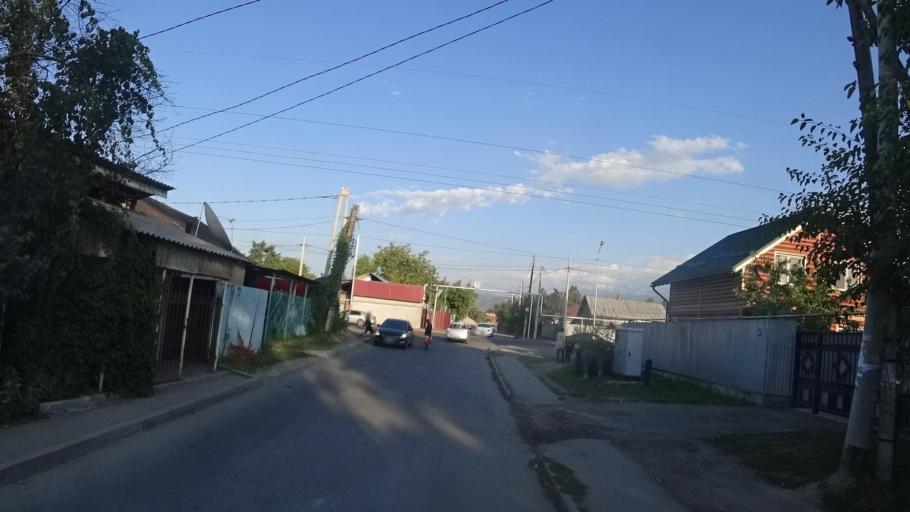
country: KZ
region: Almaty Qalasy
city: Almaty
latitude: 43.3073
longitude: 76.9664
